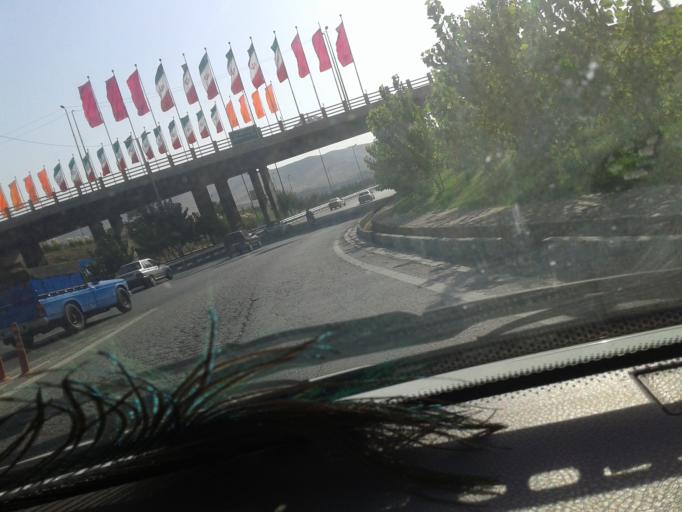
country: IR
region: Tehran
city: Tehran
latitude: 35.7248
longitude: 51.5868
